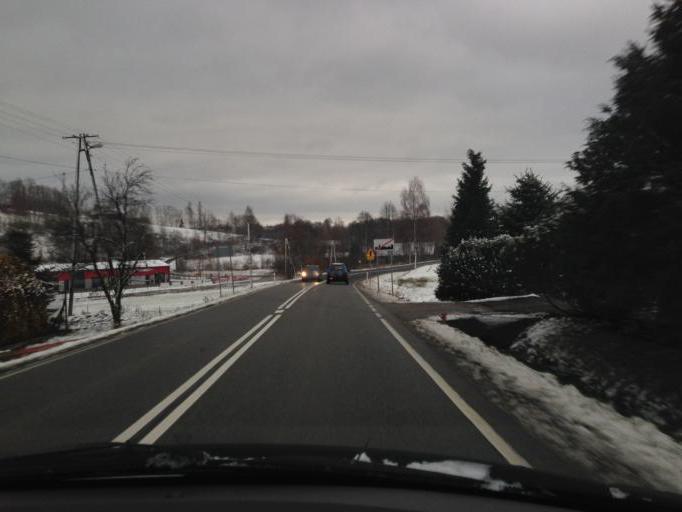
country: PL
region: Lesser Poland Voivodeship
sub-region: Powiat tarnowski
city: Siemiechow
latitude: 49.8496
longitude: 20.9272
